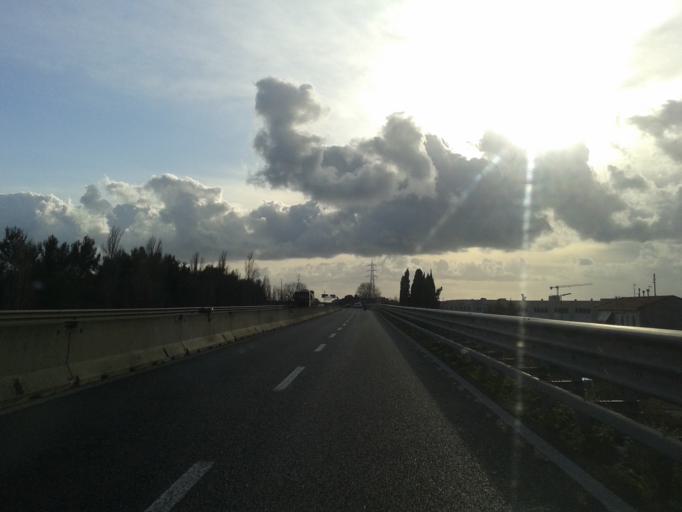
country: IT
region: Tuscany
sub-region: Provincia di Livorno
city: Livorno
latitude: 43.5384
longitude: 10.3363
